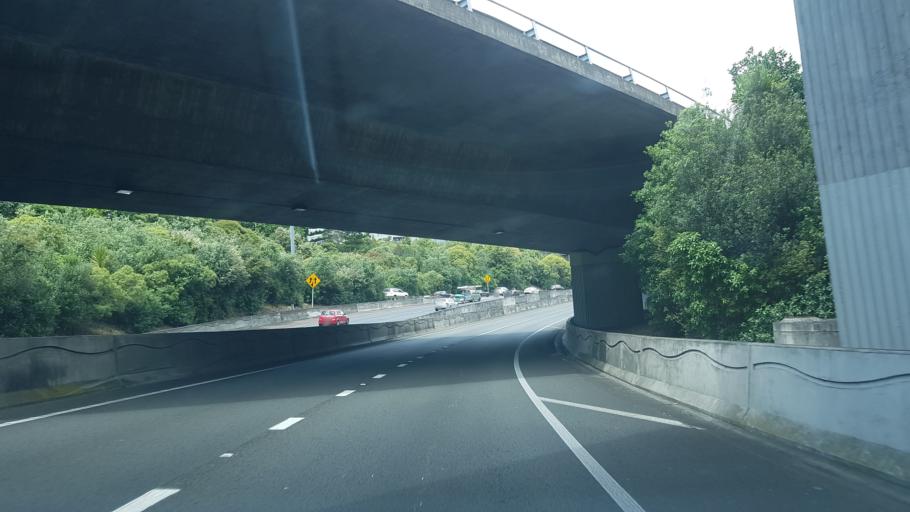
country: NZ
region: Auckland
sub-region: Auckland
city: Auckland
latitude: -36.8551
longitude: 174.7573
